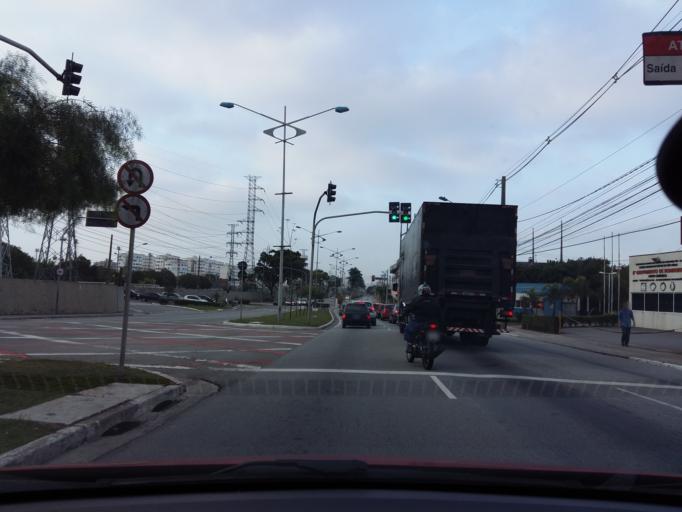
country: BR
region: Sao Paulo
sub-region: Sao Caetano Do Sul
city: Sao Caetano do Sul
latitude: -23.6229
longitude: -46.5819
